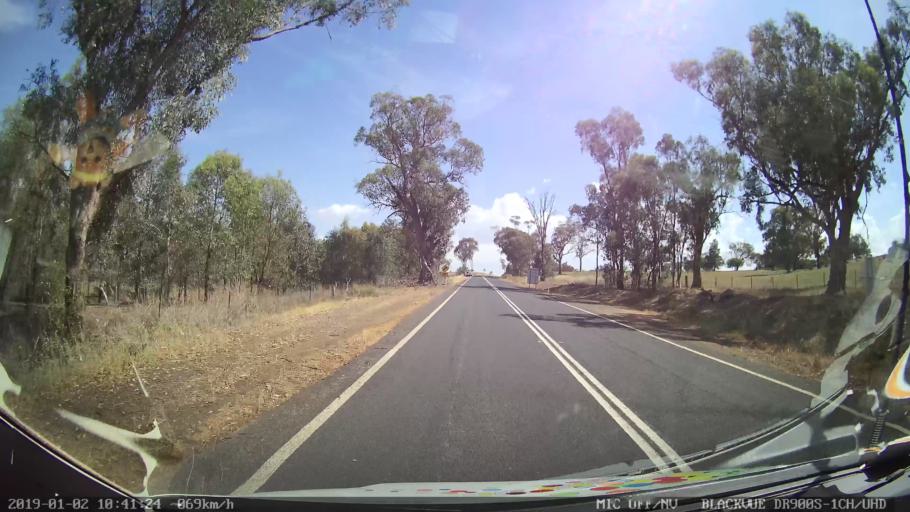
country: AU
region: New South Wales
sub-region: Cootamundra
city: Cootamundra
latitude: -34.7944
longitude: 148.3065
